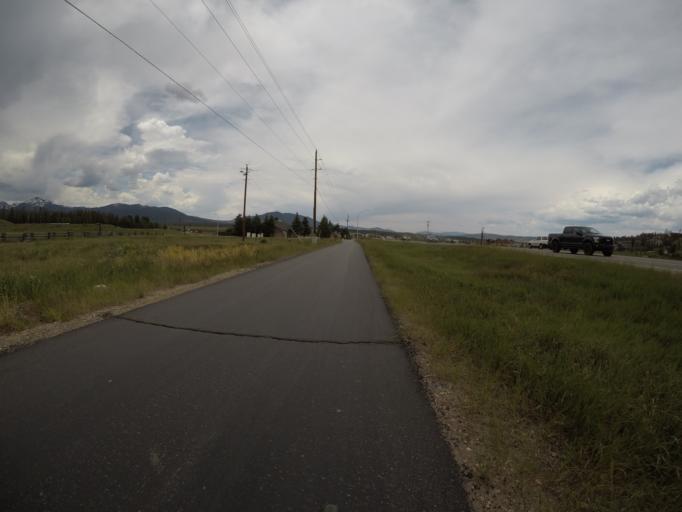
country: US
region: Colorado
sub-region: Grand County
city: Fraser
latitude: 39.9413
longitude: -105.8066
